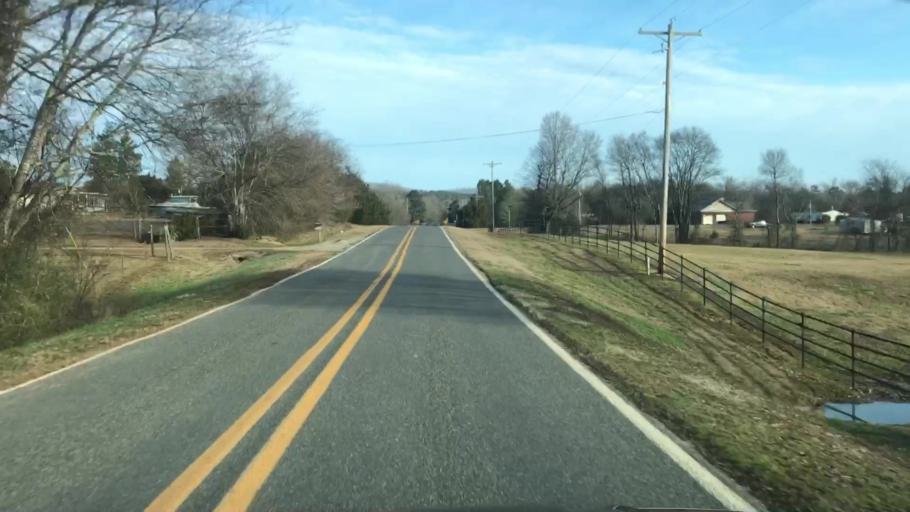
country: US
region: Arkansas
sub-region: Garland County
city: Rockwell
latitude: 34.5038
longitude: -93.2762
